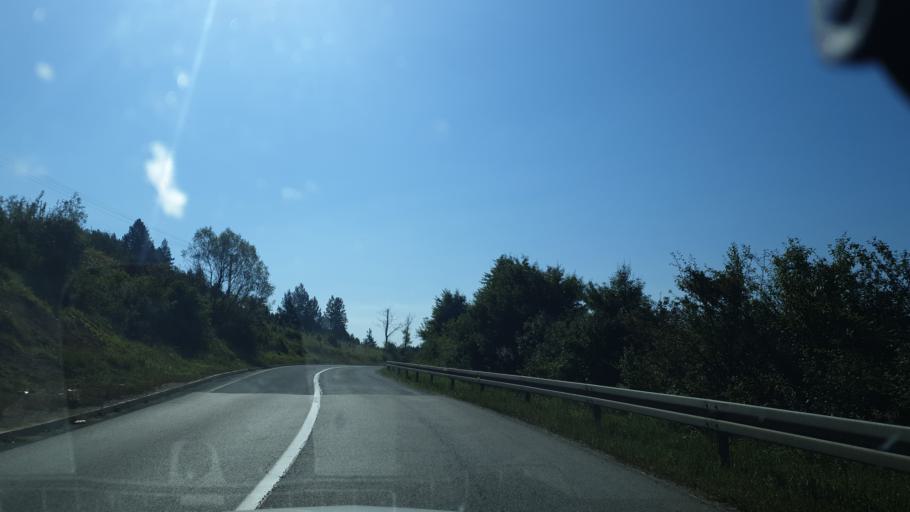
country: RS
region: Central Serbia
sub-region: Zlatiborski Okrug
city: Nova Varos
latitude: 43.5478
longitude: 19.7819
